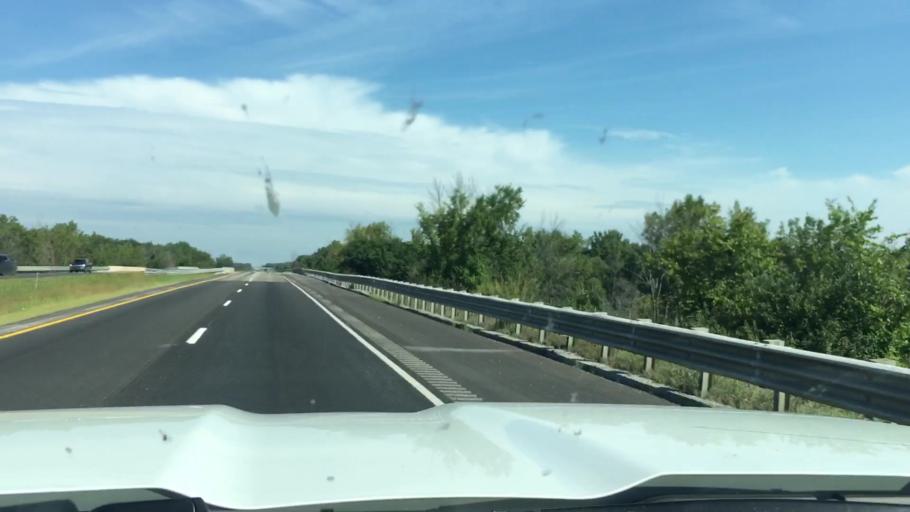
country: US
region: Michigan
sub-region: Saginaw County
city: Freeland
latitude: 43.5420
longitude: -84.1387
